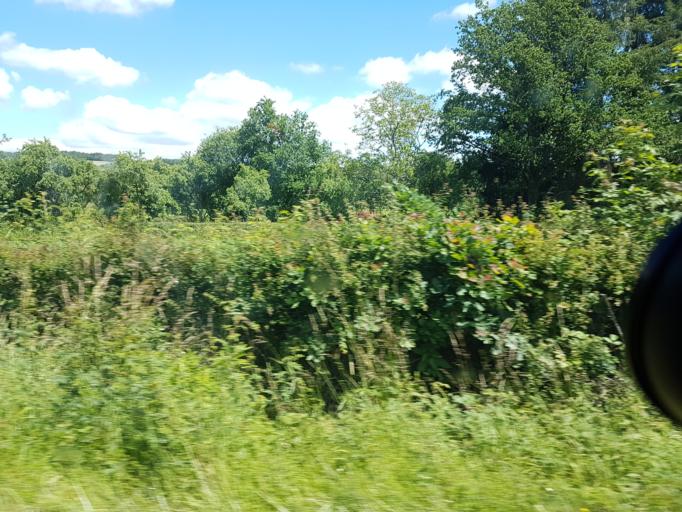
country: FR
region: Bourgogne
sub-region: Departement de Saone-et-Loire
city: Curgy
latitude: 47.0545
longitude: 4.3393
